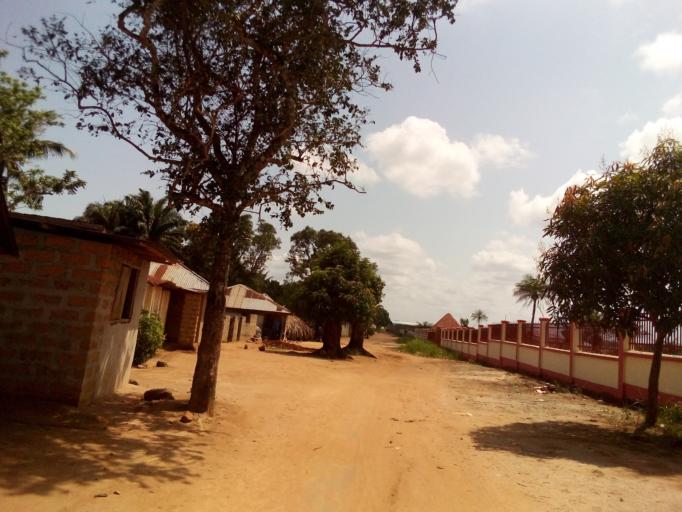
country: SL
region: Western Area
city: Waterloo
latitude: 8.3502
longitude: -13.0182
